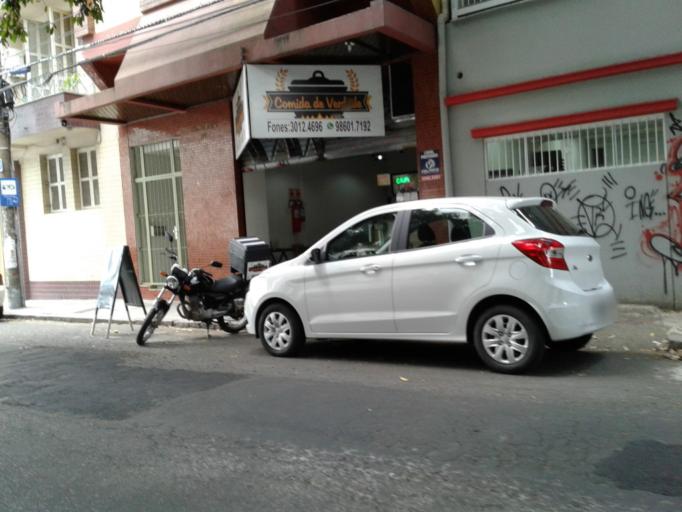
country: BR
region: Rio Grande do Sul
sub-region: Porto Alegre
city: Porto Alegre
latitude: -30.0343
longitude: -51.2231
